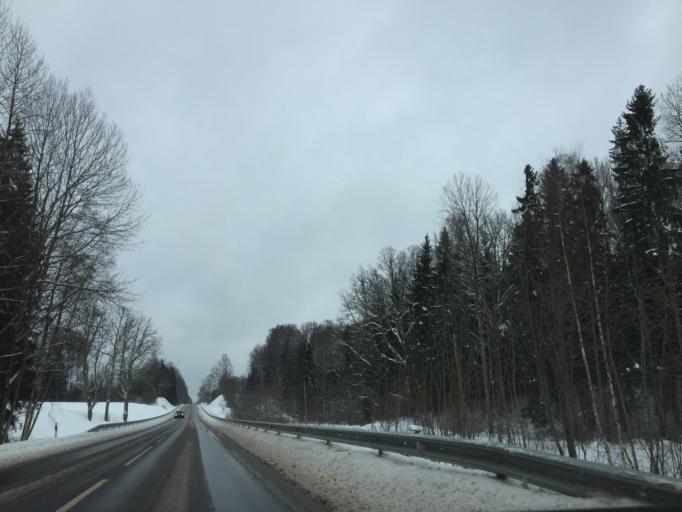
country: LV
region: Ligatne
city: Ligatne
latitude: 57.1325
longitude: 25.0858
